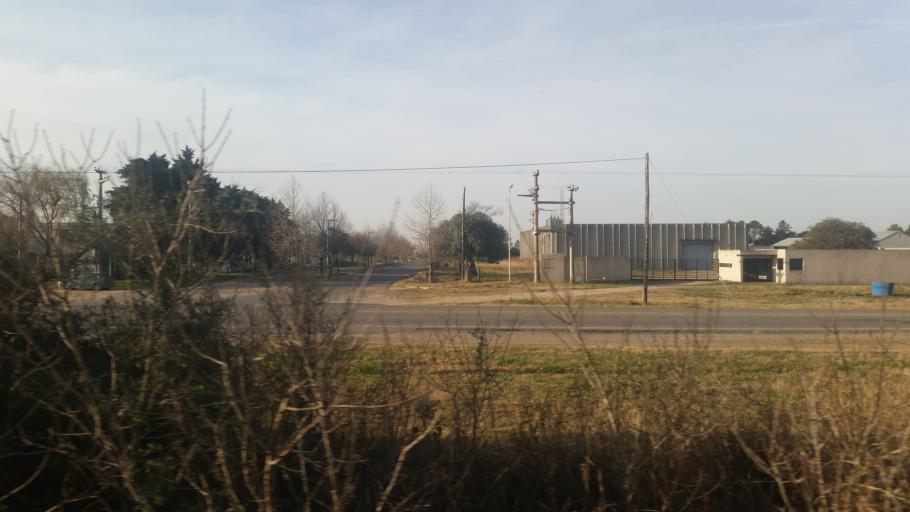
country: AR
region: Cordoba
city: Toledo
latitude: -31.5650
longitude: -64.0003
